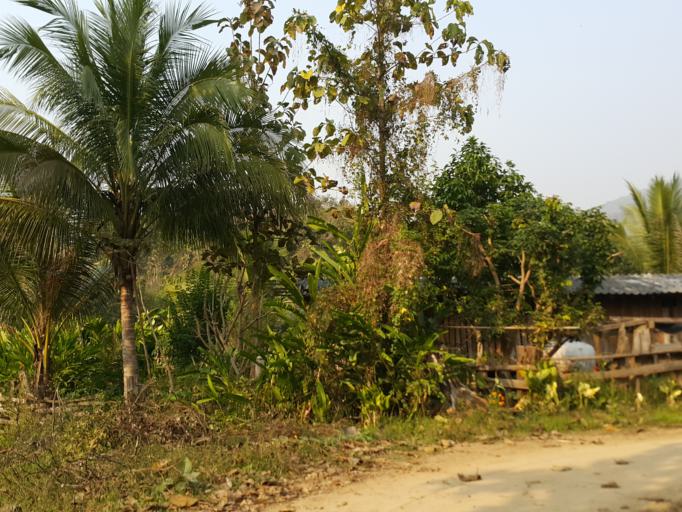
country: TH
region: Lamphun
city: Li
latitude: 17.6052
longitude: 98.9635
